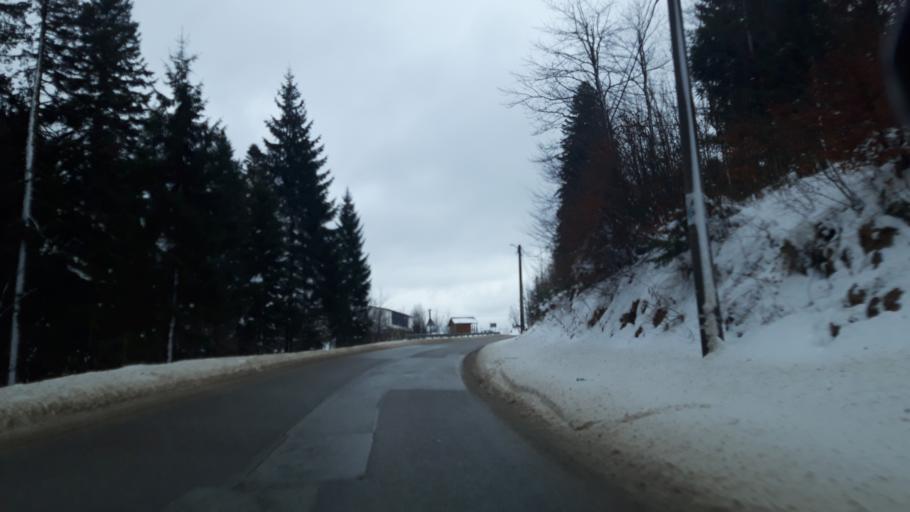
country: BA
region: Republika Srpska
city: Han Pijesak
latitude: 44.0865
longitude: 18.9533
